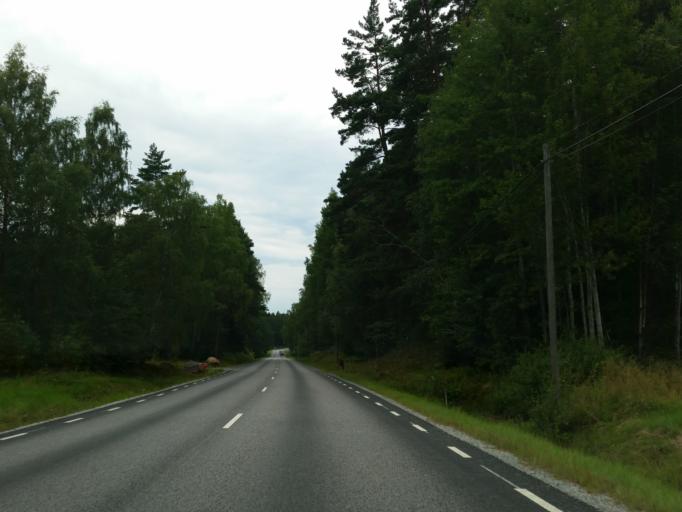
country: SE
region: Stockholm
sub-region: Salems Kommun
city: Ronninge
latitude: 59.2261
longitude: 17.6821
